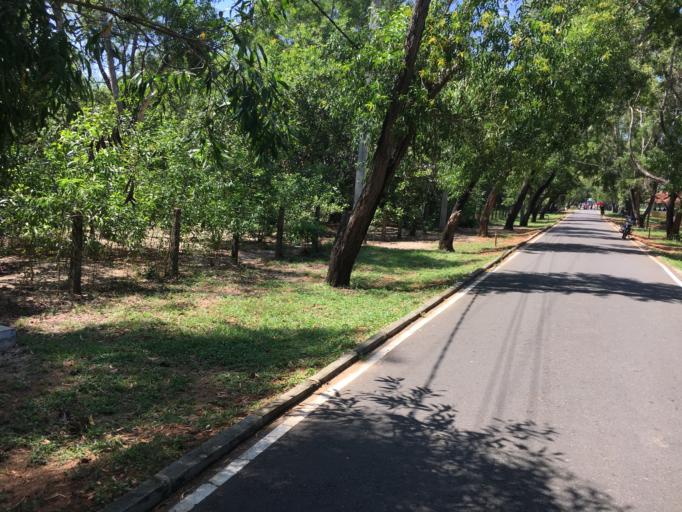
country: LK
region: Eastern Province
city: Eravur Town
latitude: 7.7970
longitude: 81.5829
